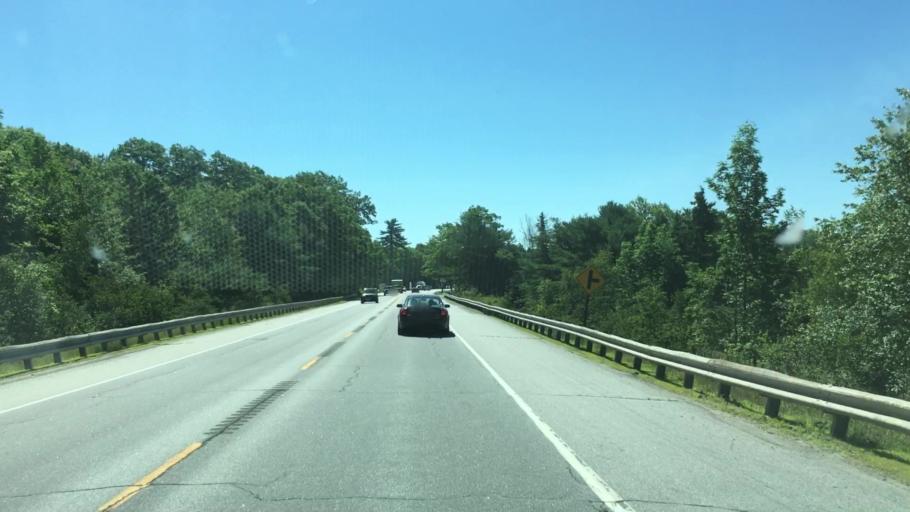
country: US
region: Maine
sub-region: Hancock County
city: Orland
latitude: 44.5679
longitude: -68.7210
